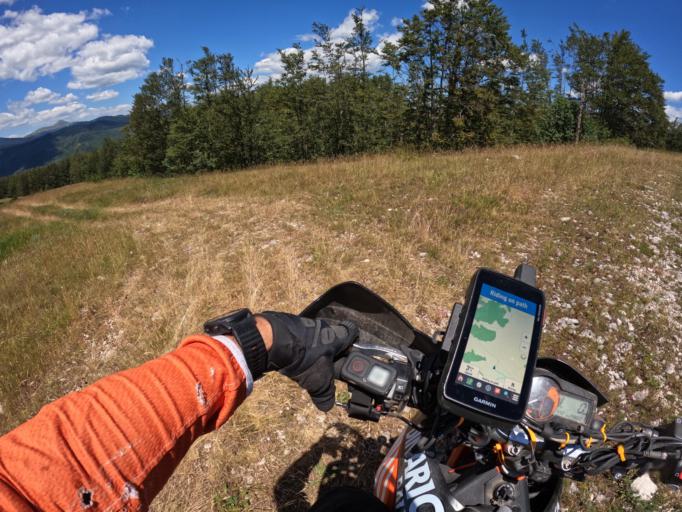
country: BA
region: Federation of Bosnia and Herzegovina
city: Tomislavgrad
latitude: 43.8561
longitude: 17.2204
